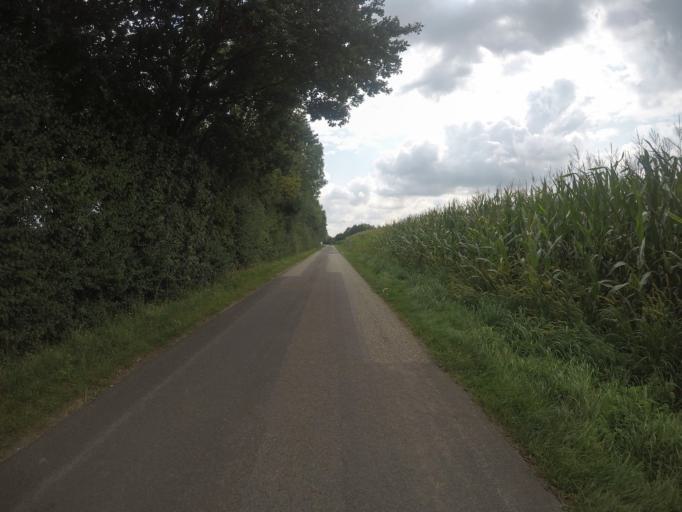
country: DE
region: North Rhine-Westphalia
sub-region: Regierungsbezirk Munster
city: Isselburg
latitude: 51.8228
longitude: 6.4943
